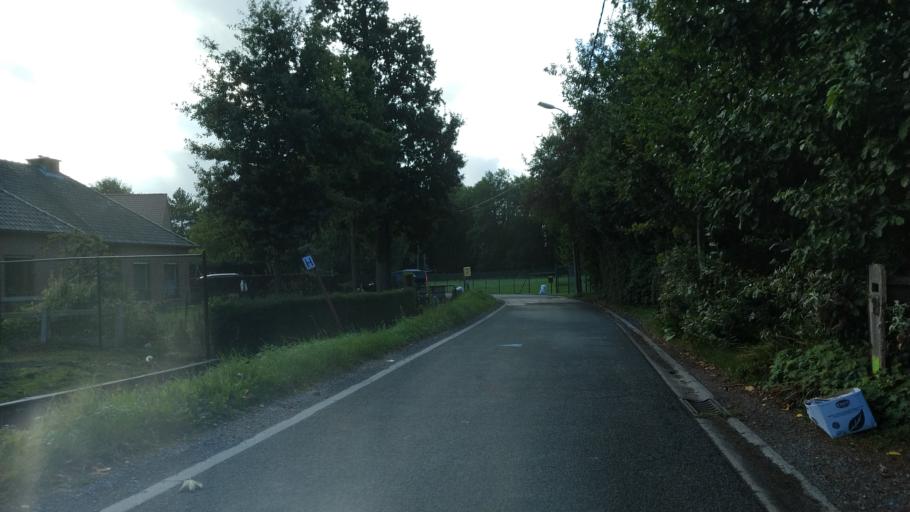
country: BE
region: Flanders
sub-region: Provincie Oost-Vlaanderen
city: Nevele
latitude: 51.0593
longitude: 3.5792
